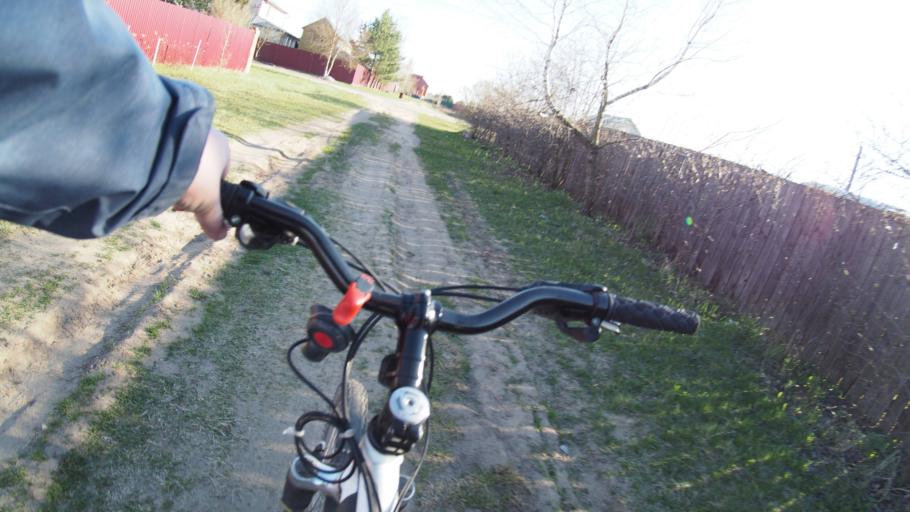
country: RU
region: Moskovskaya
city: Malyshevo
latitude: 55.5045
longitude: 38.3327
